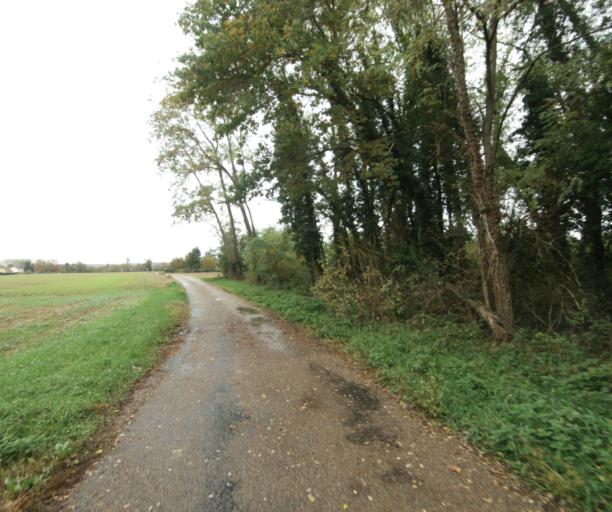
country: FR
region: Rhone-Alpes
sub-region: Departement de l'Ain
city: Pont-de-Vaux
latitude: 46.4643
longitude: 4.8993
